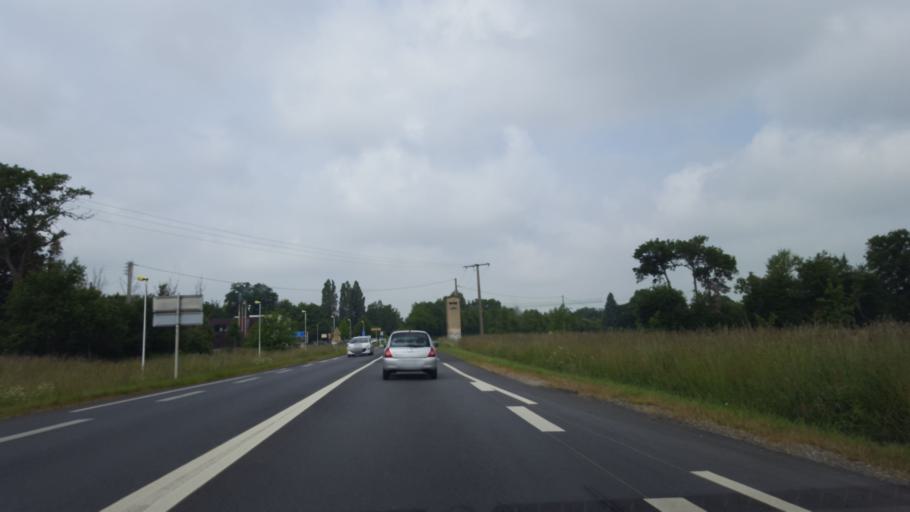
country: FR
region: Brittany
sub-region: Departement d'Ille-et-Vilaine
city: Chartres-de-Bretagne
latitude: 48.0406
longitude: -1.6897
